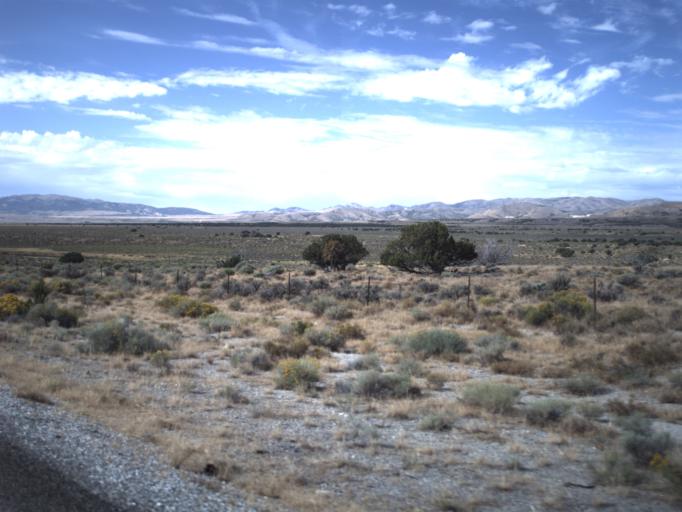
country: US
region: Idaho
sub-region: Cassia County
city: Burley
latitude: 41.6562
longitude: -113.5494
